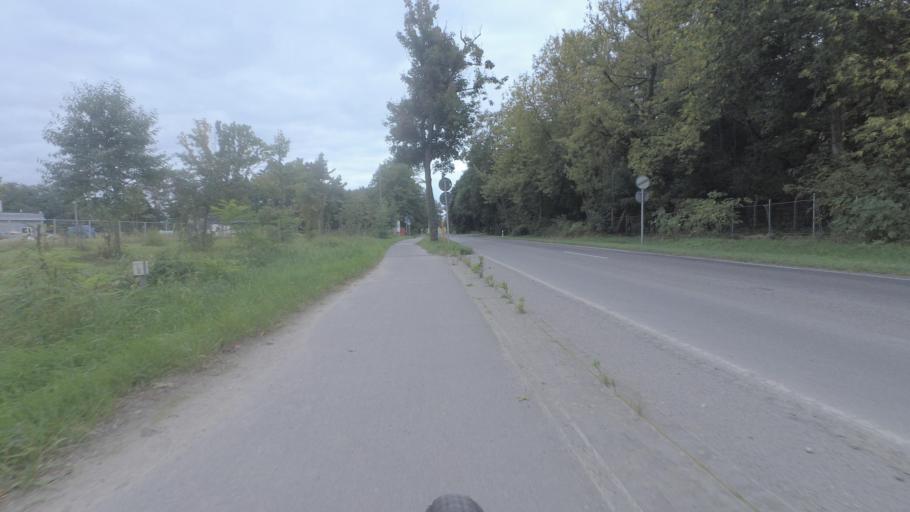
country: DE
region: Brandenburg
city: Werneuchen
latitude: 52.6098
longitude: 13.6818
